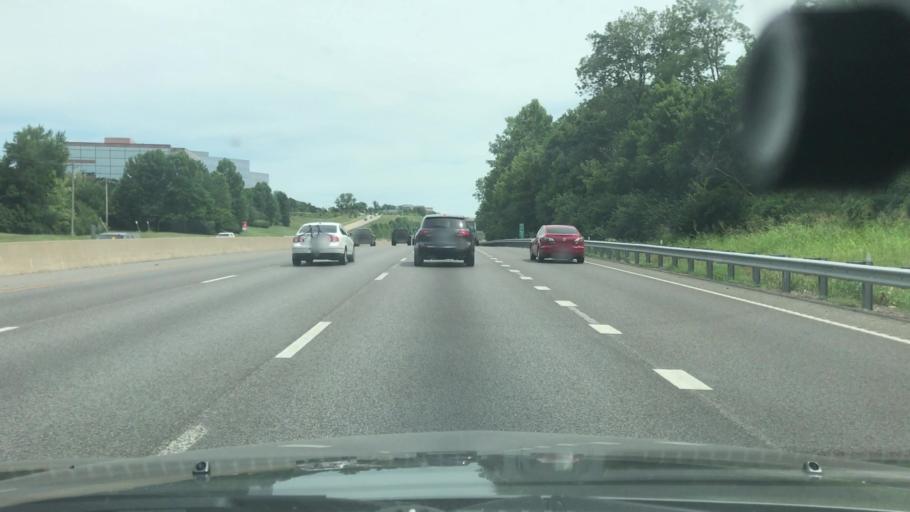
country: US
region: Missouri
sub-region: Saint Louis County
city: Chesterfield
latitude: 38.6640
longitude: -90.5722
